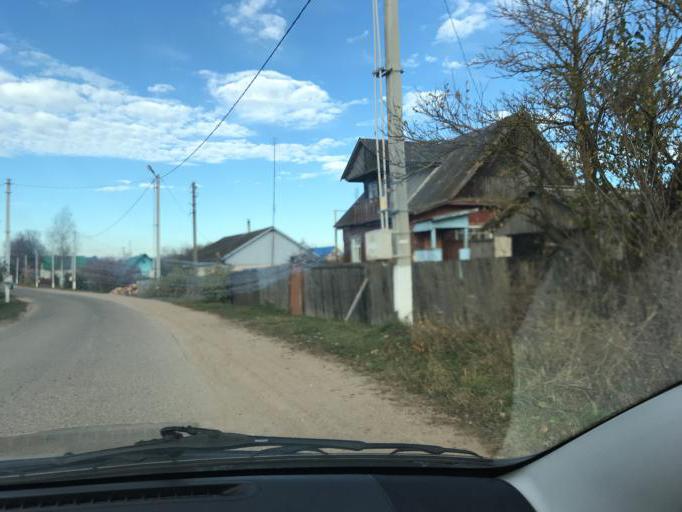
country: BY
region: Vitebsk
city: Haradok
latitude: 55.4605
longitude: 30.0047
